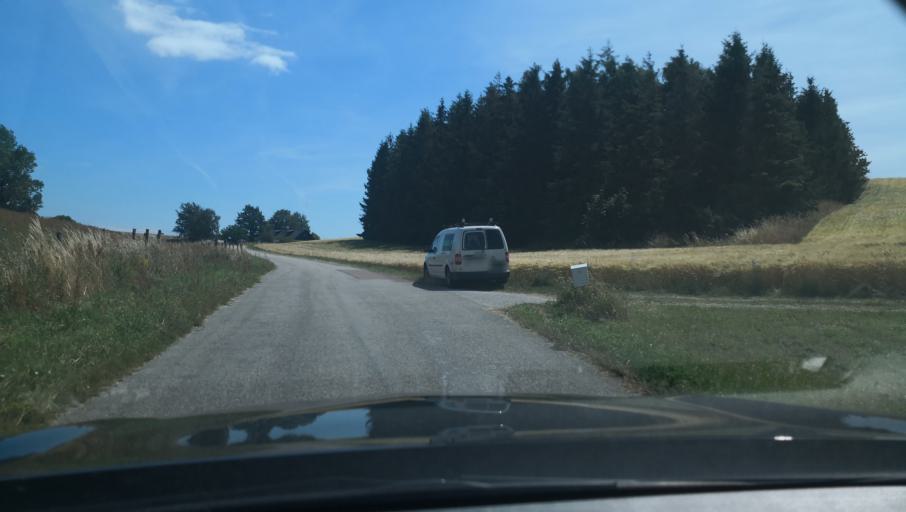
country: SE
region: Skane
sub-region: Ystads Kommun
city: Kopingebro
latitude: 55.3911
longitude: 14.1396
